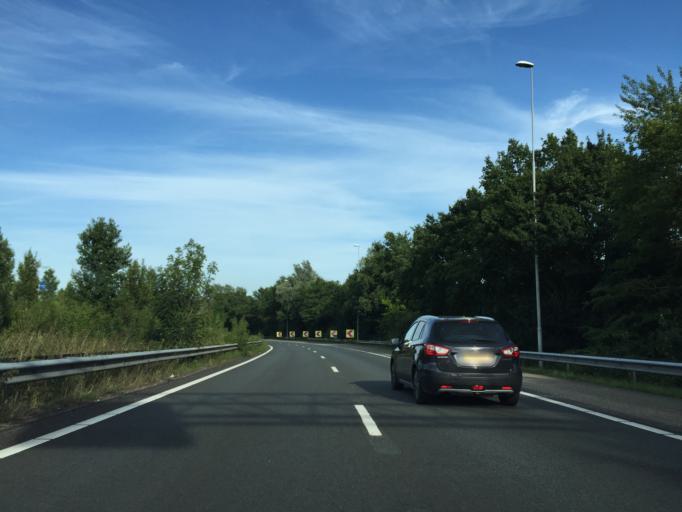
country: NL
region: North Holland
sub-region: Gemeente Amstelveen
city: Amstelveen
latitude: 52.3376
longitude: 4.8358
